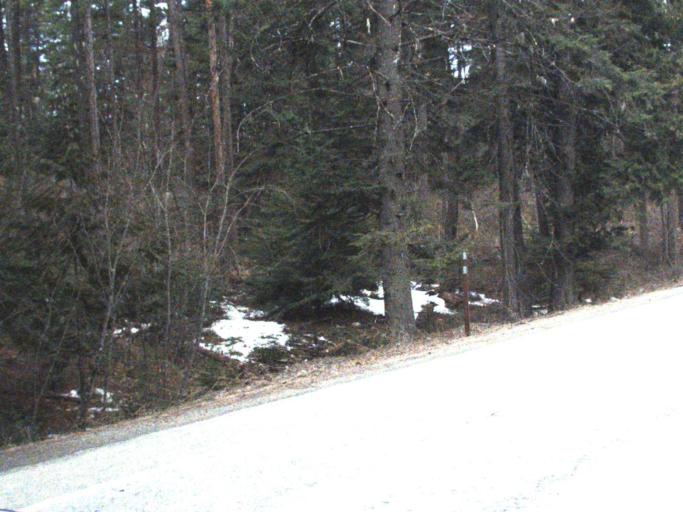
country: US
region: Washington
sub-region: Pend Oreille County
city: Newport
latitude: 48.1940
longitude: -117.0540
